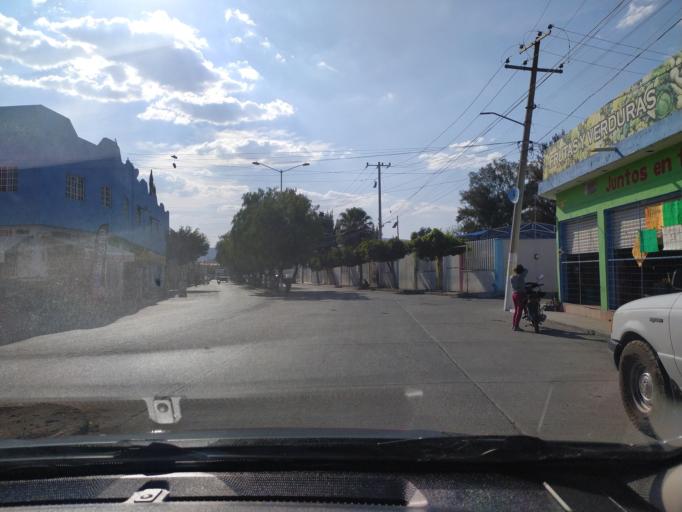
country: MX
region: Guanajuato
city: San Francisco del Rincon
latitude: 21.0174
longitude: -101.8469
